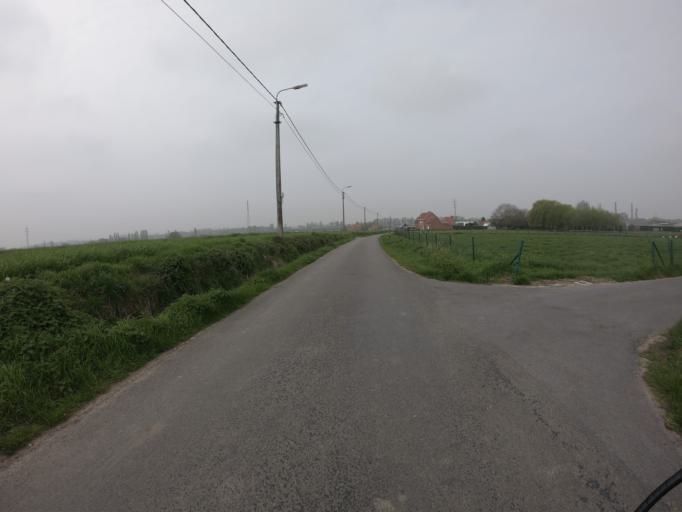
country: BE
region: Flanders
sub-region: Provincie West-Vlaanderen
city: Zwevegem
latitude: 50.8113
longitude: 3.3681
